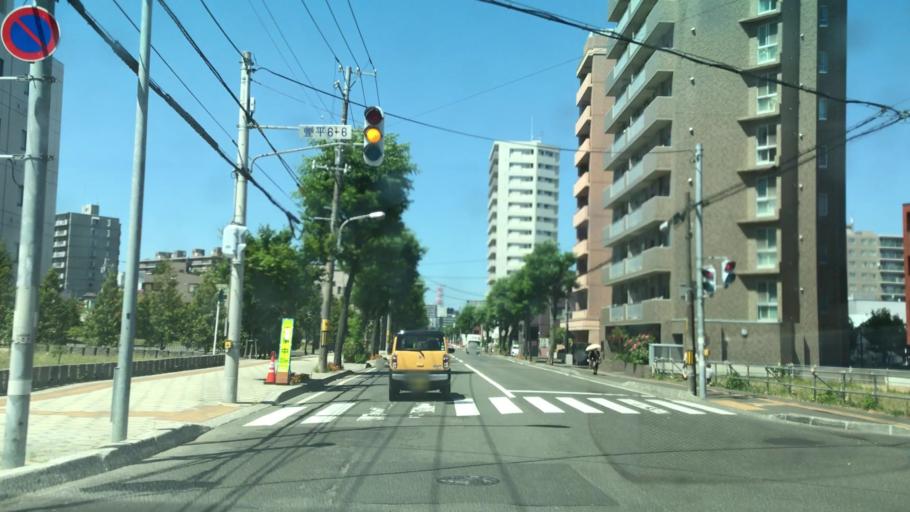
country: JP
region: Hokkaido
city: Sapporo
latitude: 43.0485
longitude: 141.3712
